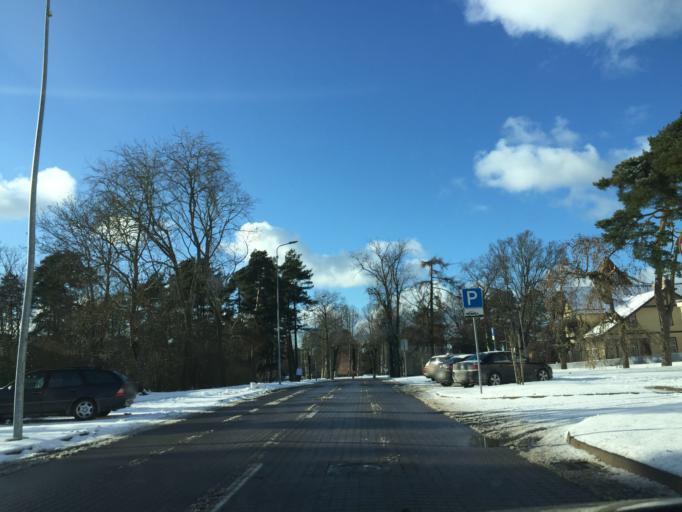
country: LV
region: Ventspils
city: Ventspils
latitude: 57.3867
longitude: 21.5438
